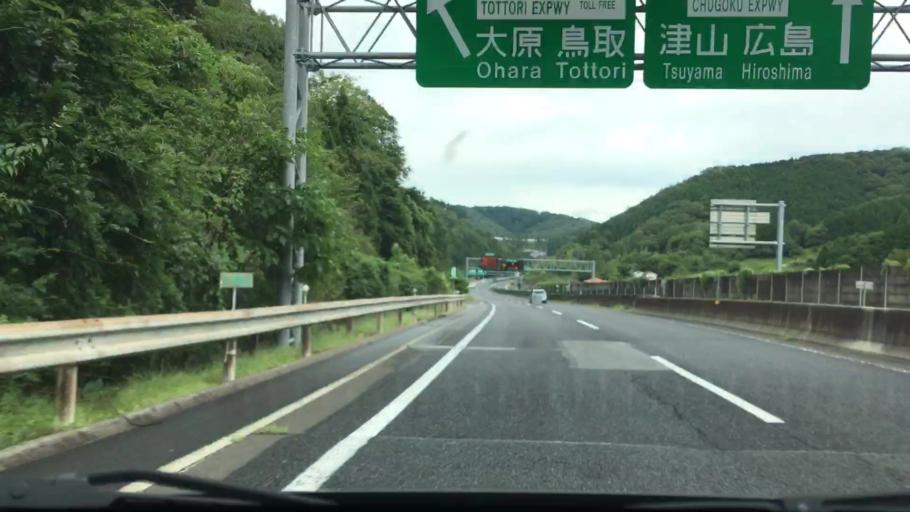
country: JP
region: Hyogo
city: Yamazakicho-nakabirose
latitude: 35.0295
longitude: 134.3983
